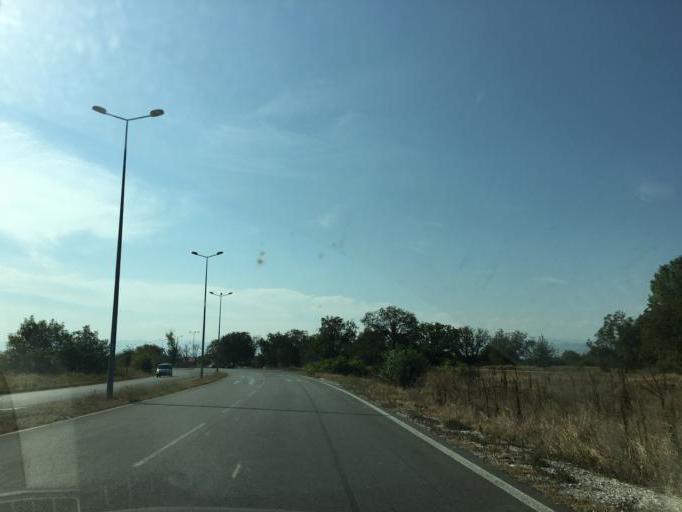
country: BG
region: Pazardzhik
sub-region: Obshtina Pazardzhik
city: Pazardzhik
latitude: 42.2232
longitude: 24.3104
